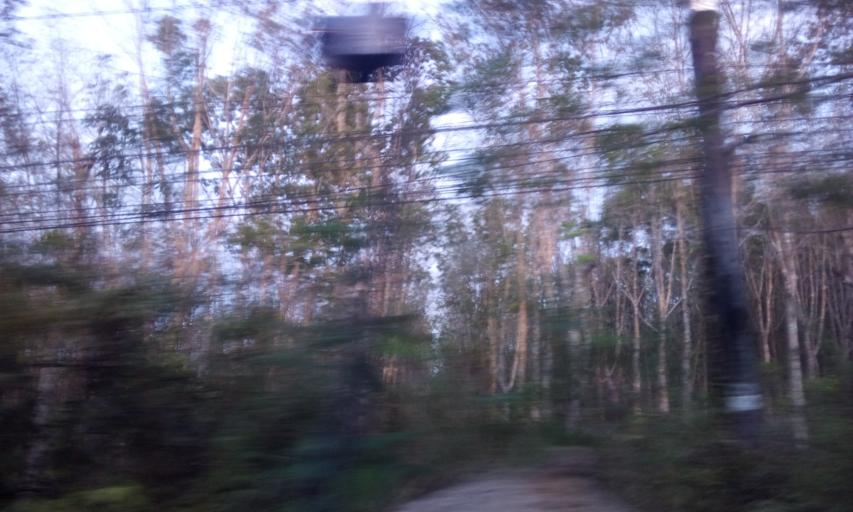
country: TH
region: Trat
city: Laem Ngop
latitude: 12.2723
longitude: 102.3057
